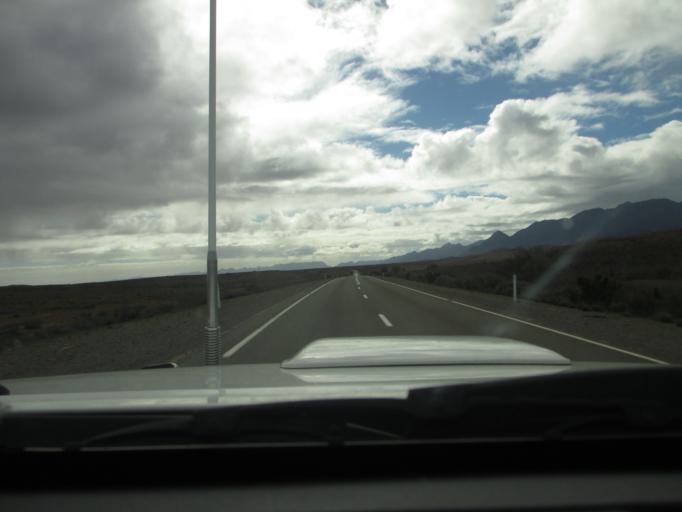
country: AU
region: South Australia
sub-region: Flinders Ranges
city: Quorn
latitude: -31.5751
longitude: 138.4215
